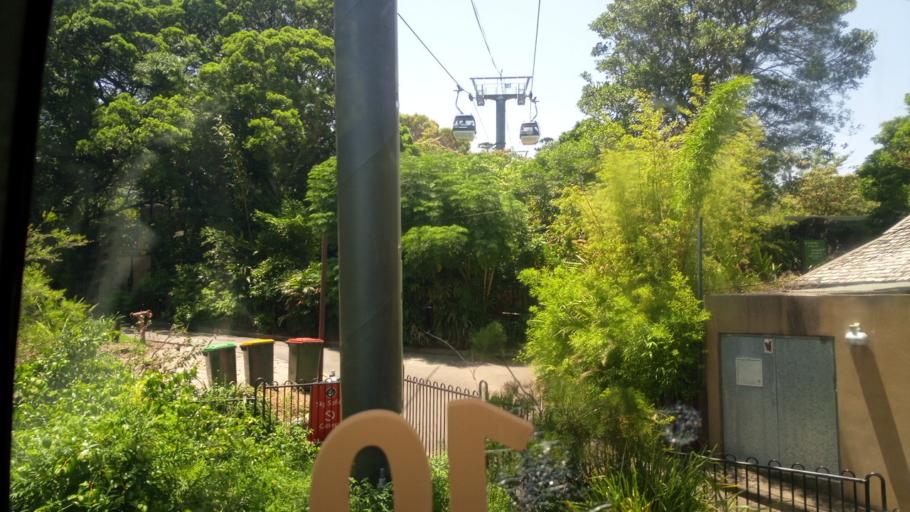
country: AU
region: New South Wales
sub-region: Mosman
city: Mosman
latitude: -33.8452
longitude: 151.2397
